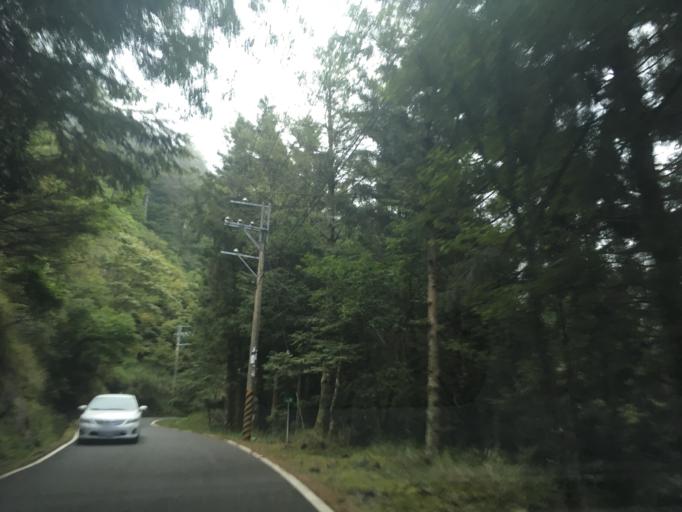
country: TW
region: Taiwan
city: Fengyuan
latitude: 24.2694
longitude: 121.0221
